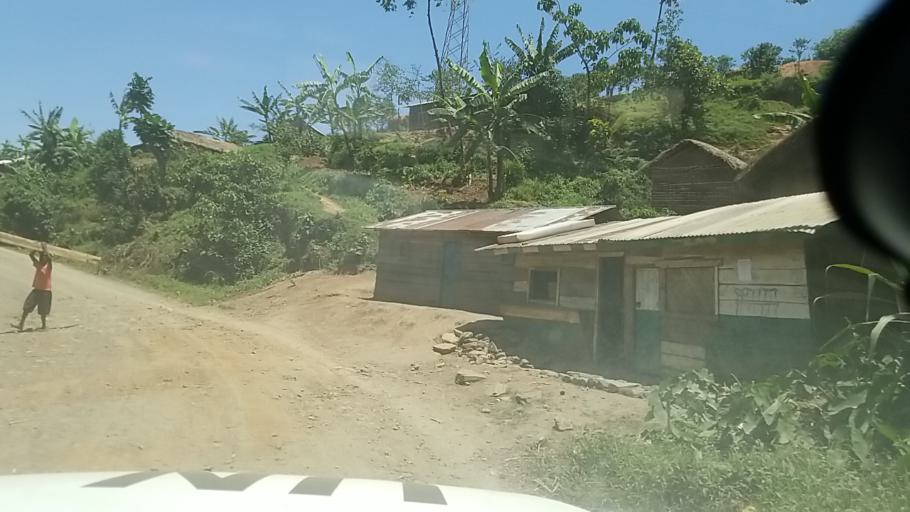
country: CD
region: Nord Kivu
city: Sake
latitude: -1.9188
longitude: 28.9449
